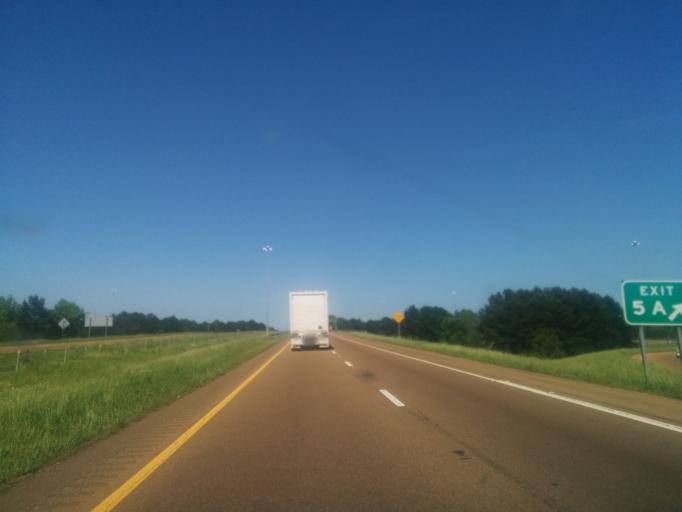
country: US
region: Mississippi
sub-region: Hinds County
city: Jackson
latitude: 32.3577
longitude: -90.2381
